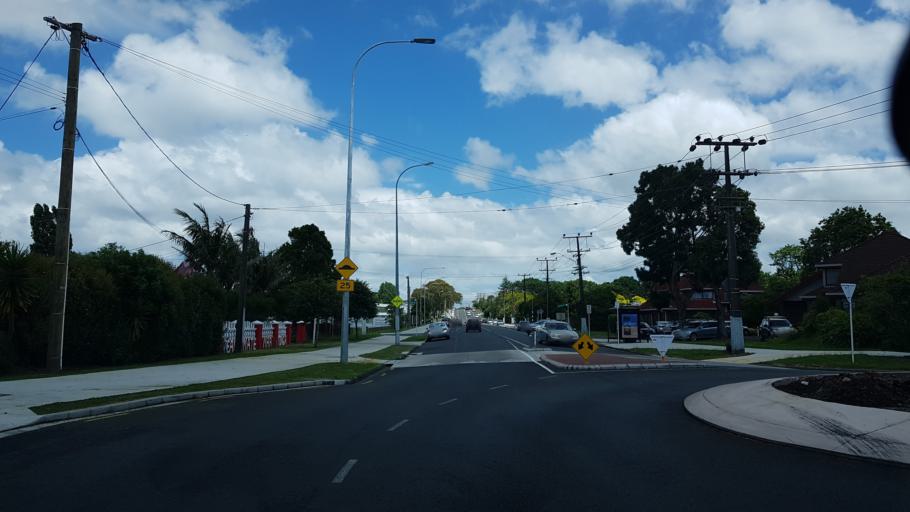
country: NZ
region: Auckland
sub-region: Auckland
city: North Shore
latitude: -36.7942
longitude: 174.7454
